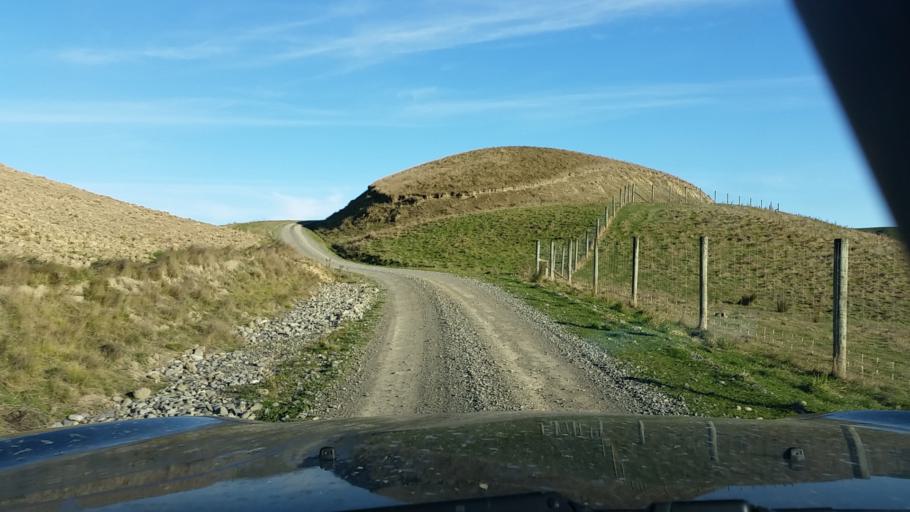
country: NZ
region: Marlborough
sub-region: Marlborough District
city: Blenheim
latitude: -41.7360
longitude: 173.9933
